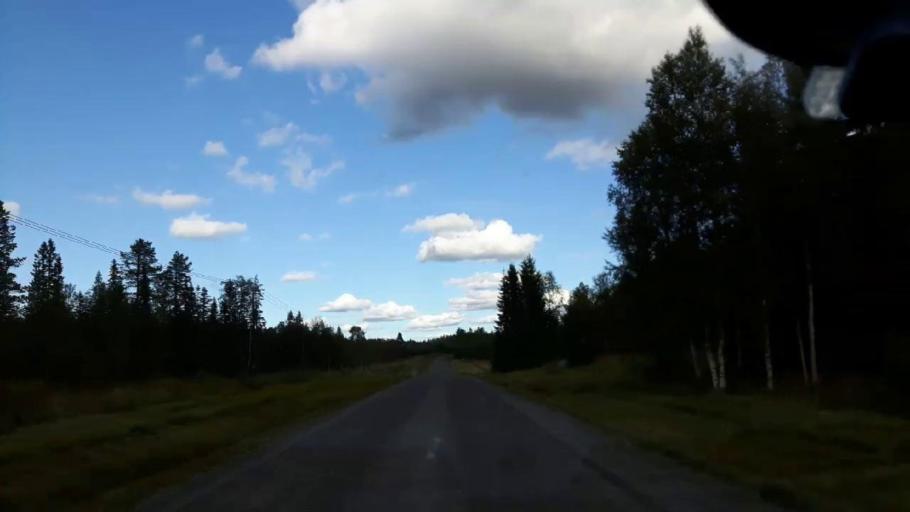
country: SE
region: Jaemtland
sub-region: Stroemsunds Kommun
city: Stroemsund
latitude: 63.4221
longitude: 15.8788
